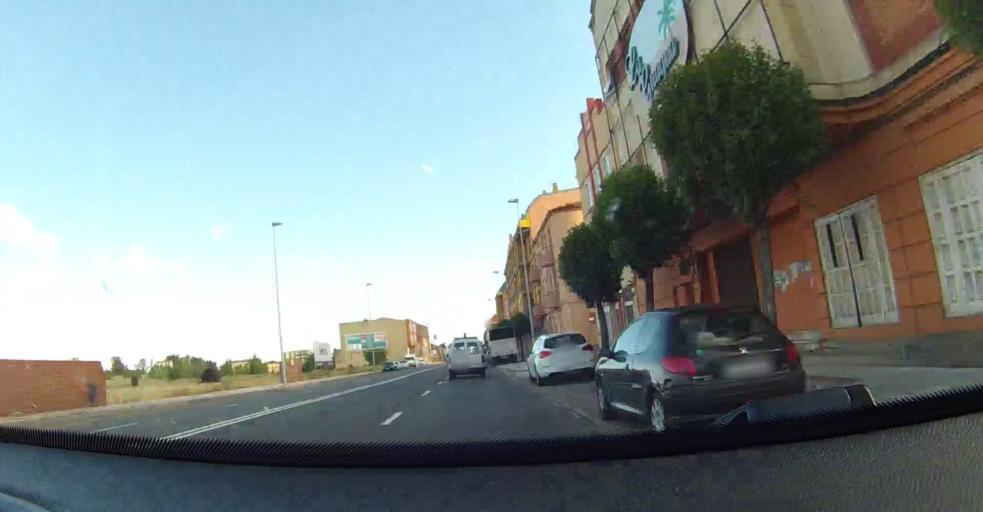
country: ES
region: Castille and Leon
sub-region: Provincia de Leon
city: Leon
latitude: 42.5888
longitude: -5.5846
